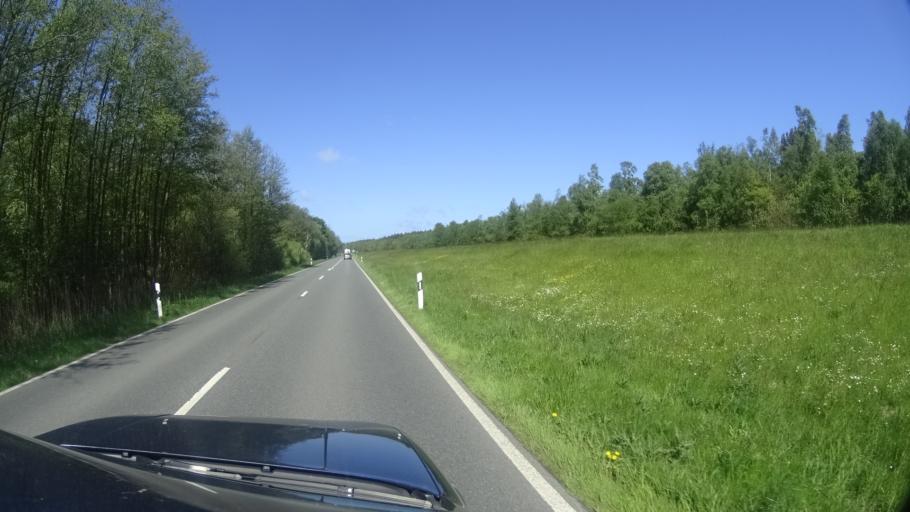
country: DE
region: Mecklenburg-Vorpommern
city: Ostseebad Prerow
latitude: 54.4456
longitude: 12.6291
